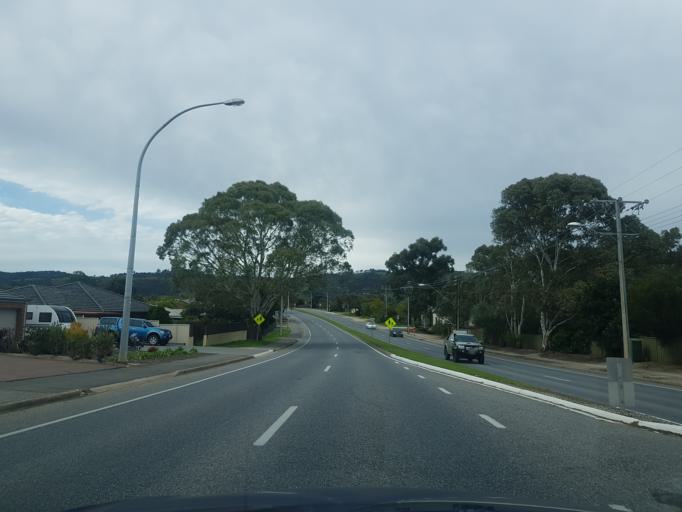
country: AU
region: South Australia
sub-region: Campbelltown
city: Athelstone
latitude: -34.8526
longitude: 138.7075
